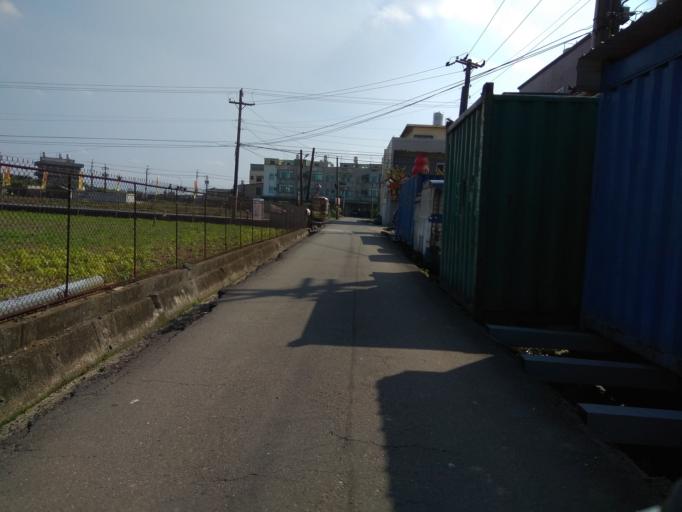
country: TW
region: Taiwan
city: Taoyuan City
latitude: 25.0500
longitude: 121.2222
